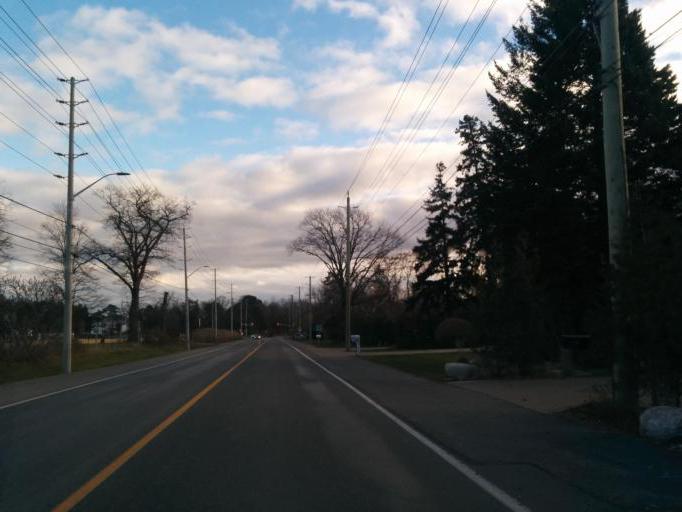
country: CA
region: Ontario
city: Oakville
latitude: 43.4851
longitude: -79.6301
